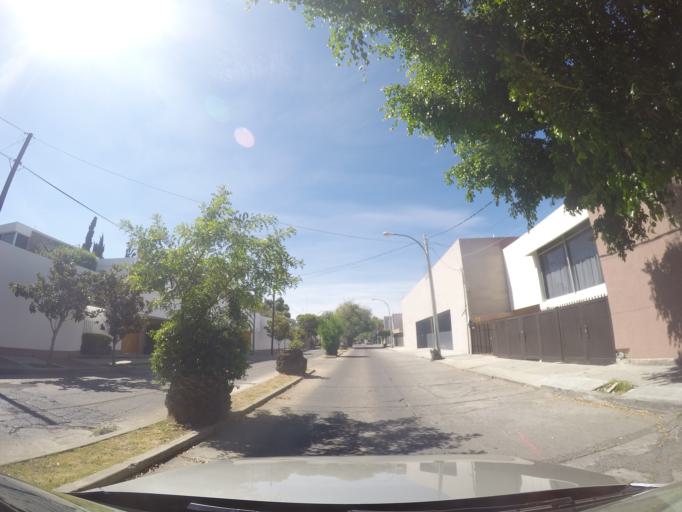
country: MX
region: San Luis Potosi
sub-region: San Luis Potosi
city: San Luis Potosi
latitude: 22.1509
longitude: -101.0108
